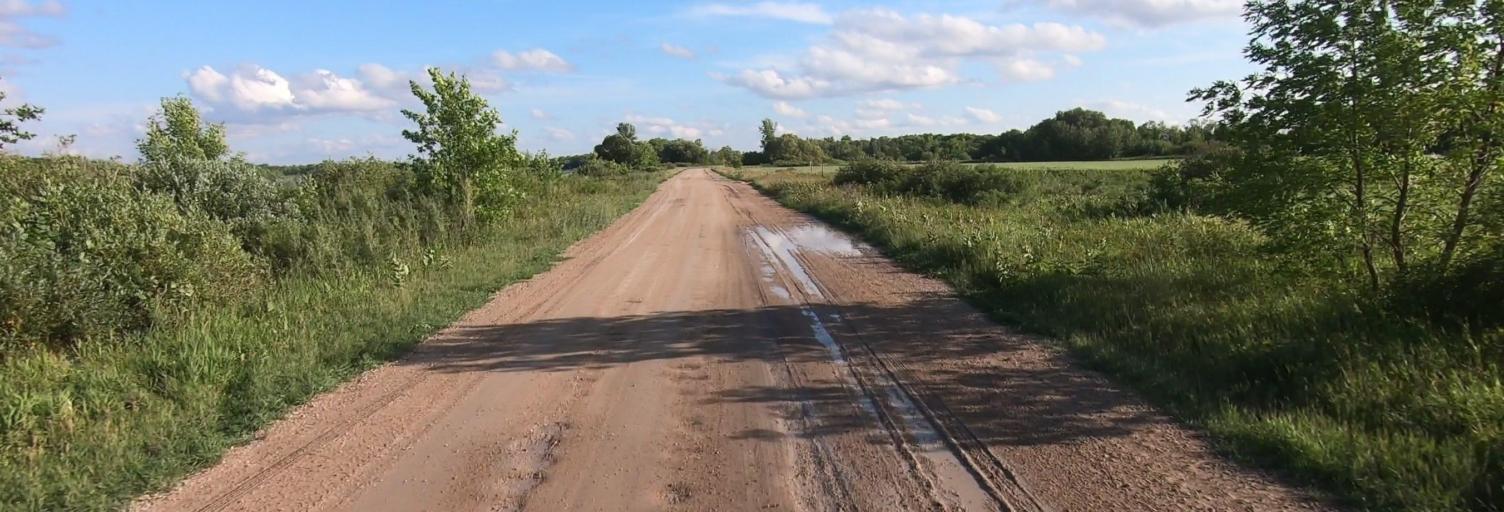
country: CA
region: Manitoba
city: Selkirk
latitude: 50.2600
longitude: -96.8495
